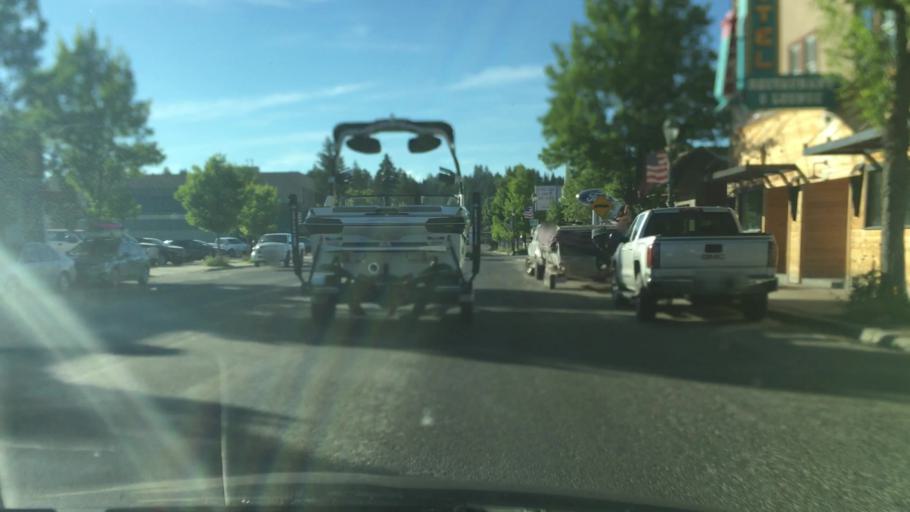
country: US
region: Idaho
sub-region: Valley County
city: Cascade
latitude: 44.5163
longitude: -116.0421
